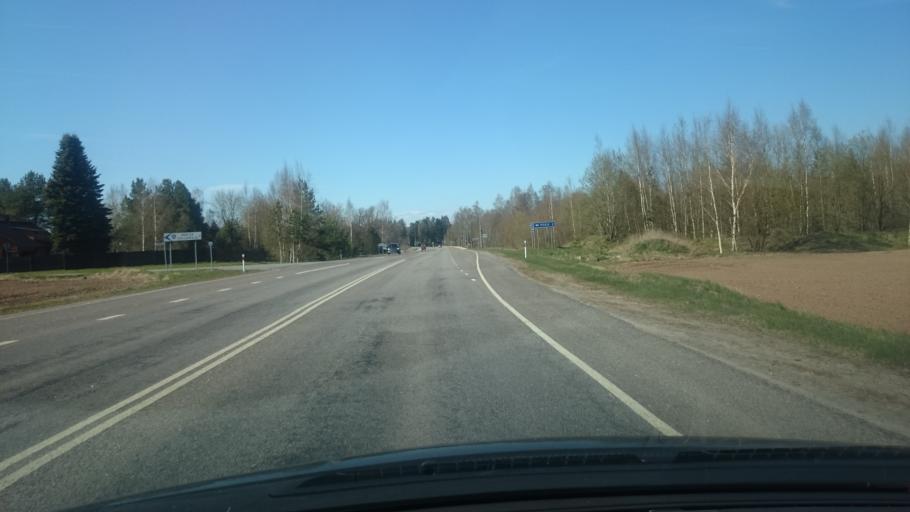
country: EE
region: Tartu
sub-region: UElenurme vald
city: Ulenurme
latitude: 58.3284
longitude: 26.9799
